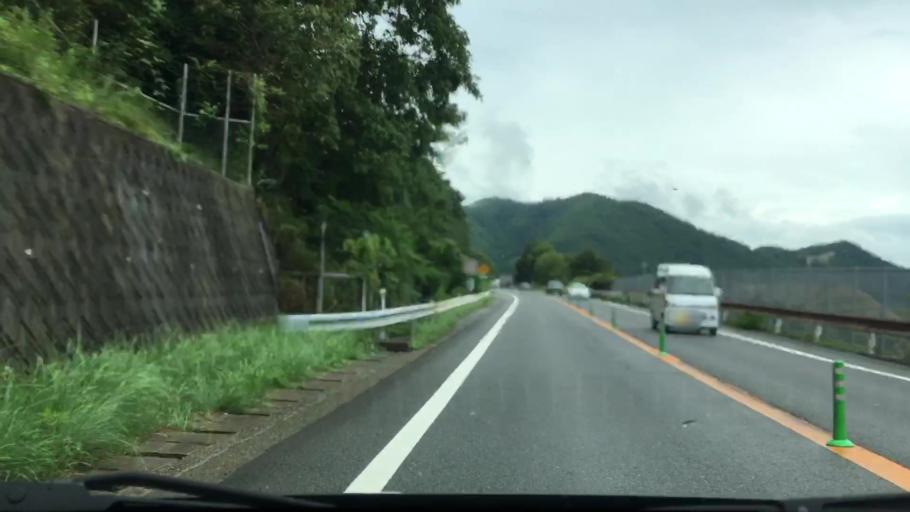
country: JP
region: Hyogo
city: Himeji
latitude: 35.0100
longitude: 134.7621
